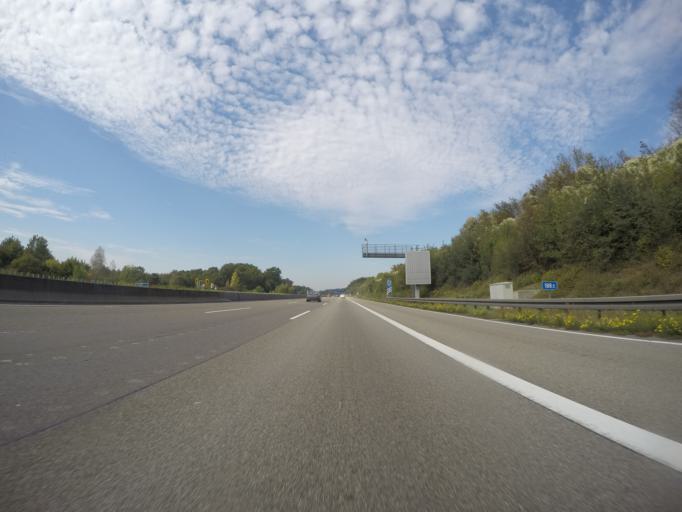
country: DE
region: Hesse
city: Obertshausen
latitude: 50.0661
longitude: 8.8328
